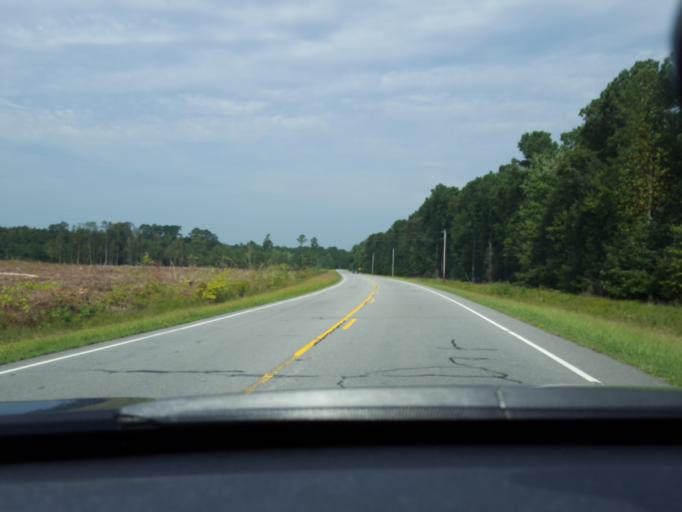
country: US
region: North Carolina
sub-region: Washington County
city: Plymouth
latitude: 35.9677
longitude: -76.7518
